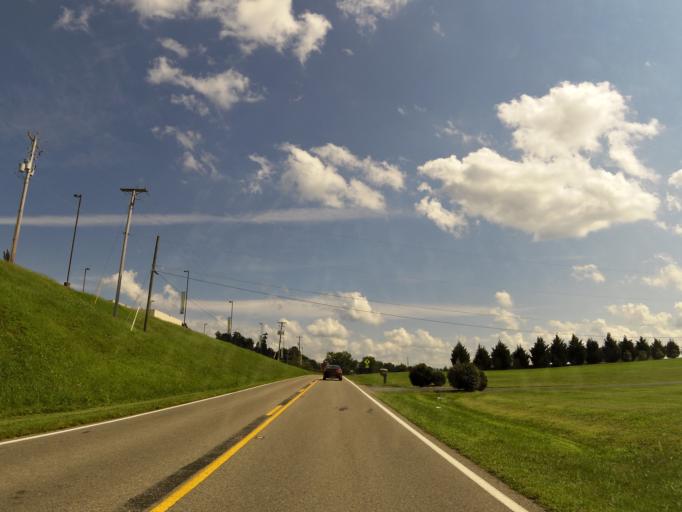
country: US
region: Virginia
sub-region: Washington County
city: Abingdon
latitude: 36.6678
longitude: -81.9673
